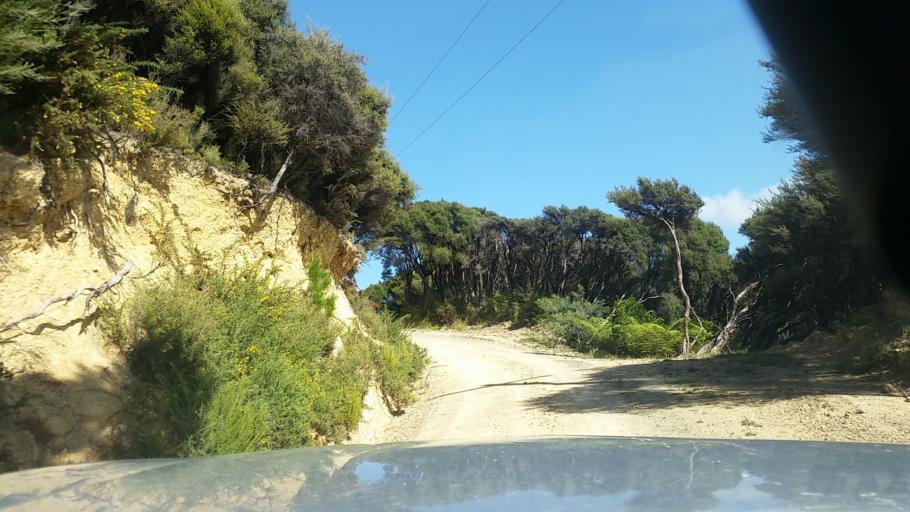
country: NZ
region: Marlborough
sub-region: Marlborough District
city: Picton
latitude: -41.3078
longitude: 174.1719
